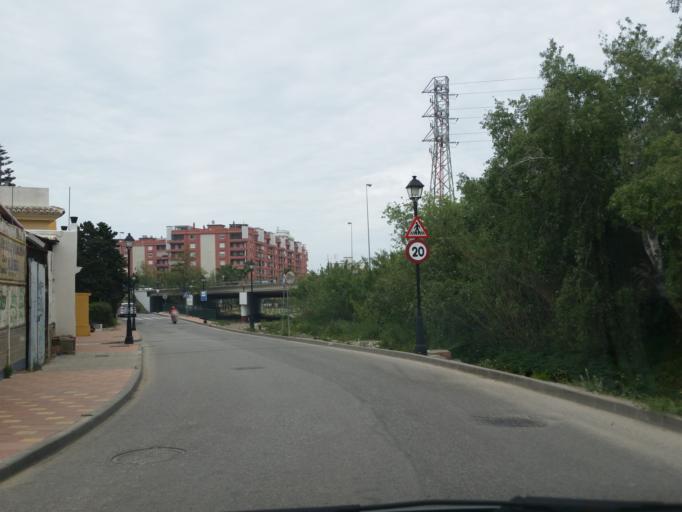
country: ES
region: Andalusia
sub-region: Provincia de Malaga
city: Fuengirola
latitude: 36.5591
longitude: -4.6172
